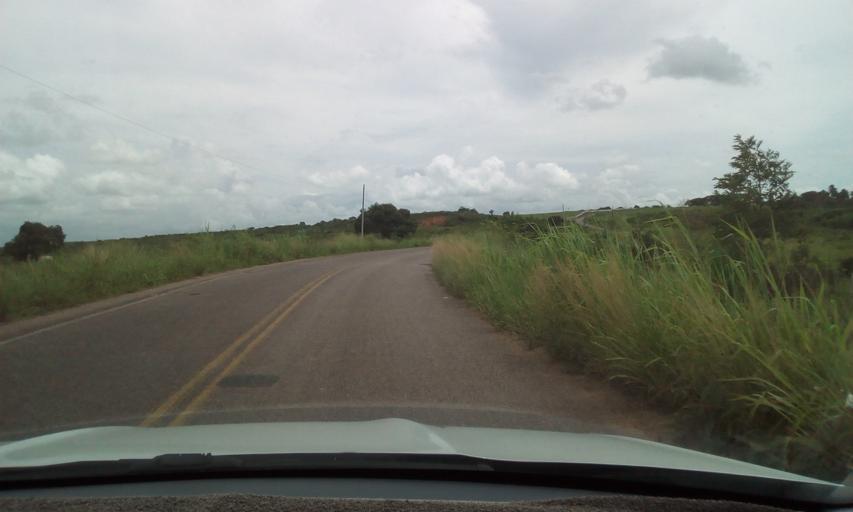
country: BR
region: Paraiba
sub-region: Mari
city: Mari
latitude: -7.0802
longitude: -35.3212
